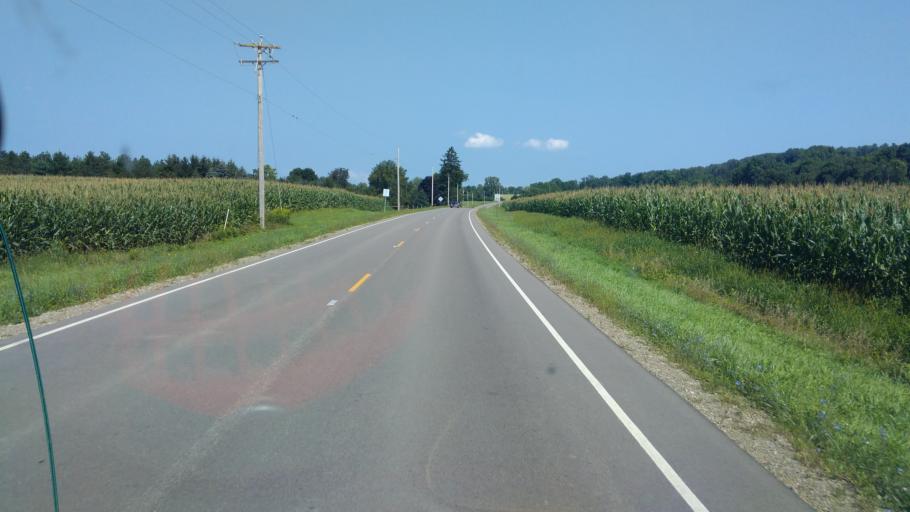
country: US
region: New York
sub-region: Allegany County
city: Belmont
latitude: 42.2434
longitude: -78.0408
